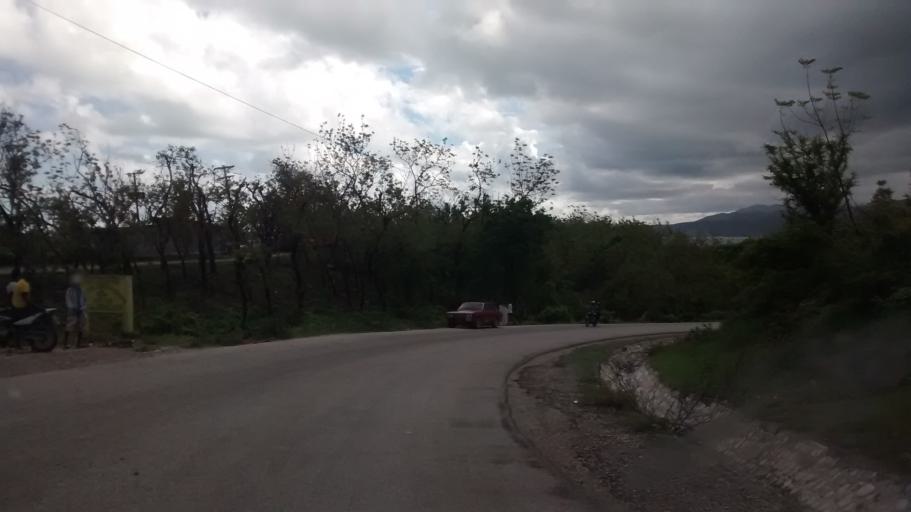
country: HT
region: Grandans
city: Jeremie
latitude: 18.6204
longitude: -74.0905
